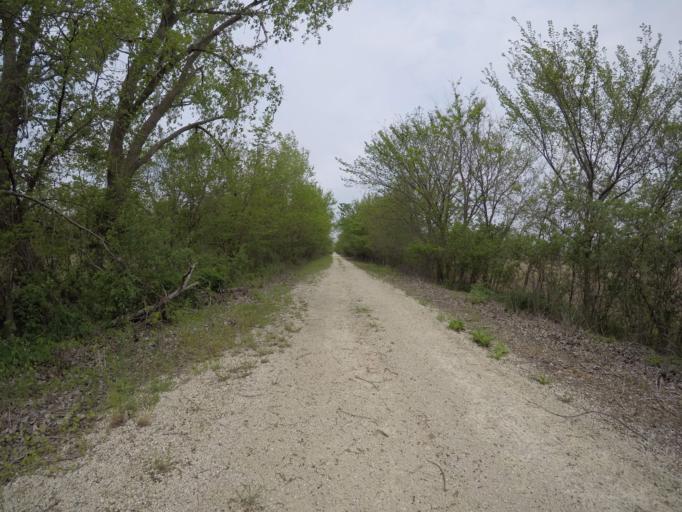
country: US
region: Nebraska
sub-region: Gage County
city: Beatrice
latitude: 40.2361
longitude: -96.6790
